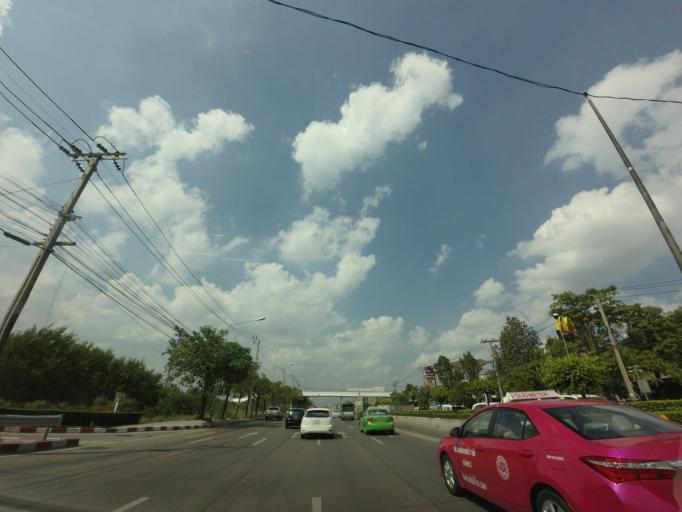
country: TH
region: Bangkok
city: Lat Phrao
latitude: 13.8328
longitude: 100.6110
